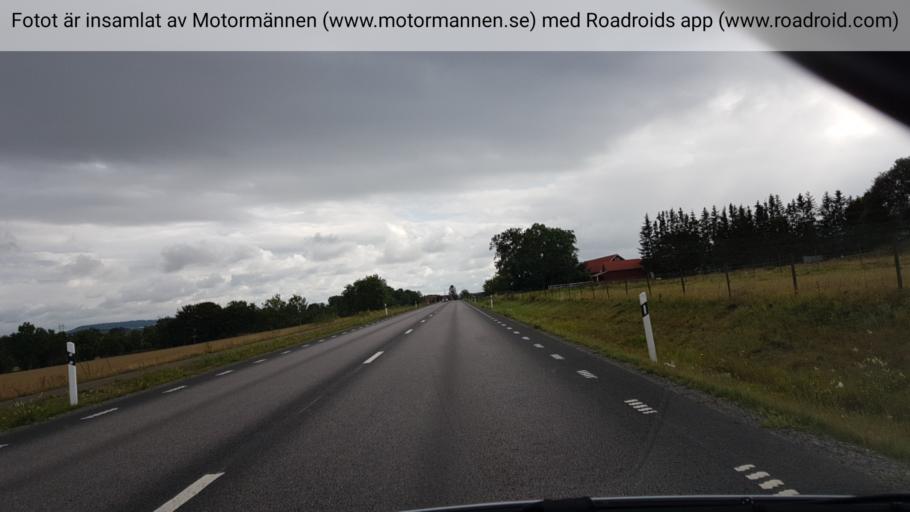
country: SE
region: Vaestra Goetaland
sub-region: Falkopings Kommun
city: Falkoeping
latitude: 58.2155
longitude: 13.5634
